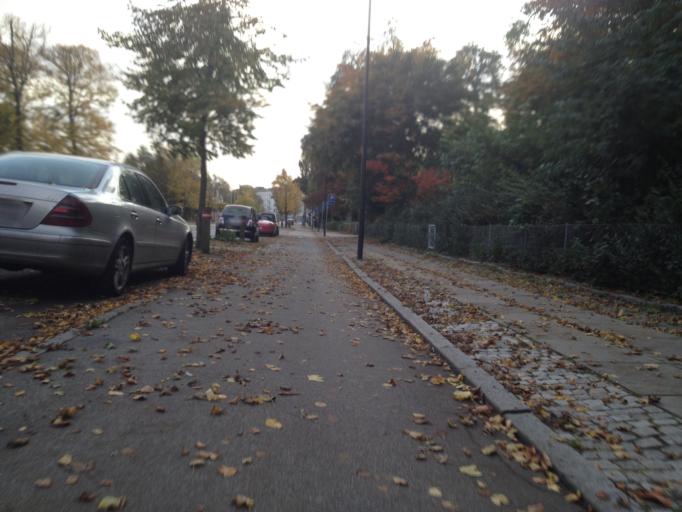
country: DK
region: Capital Region
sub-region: Gentofte Kommune
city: Charlottenlund
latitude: 55.7389
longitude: 12.5762
